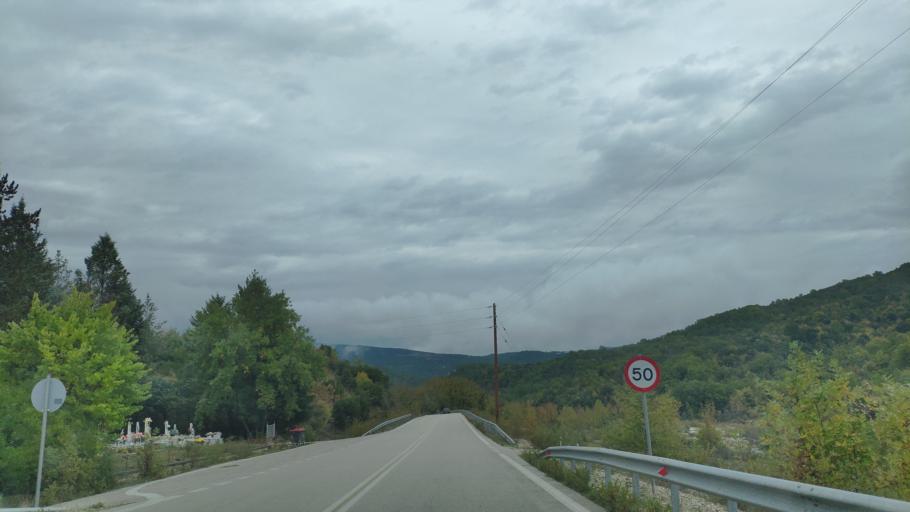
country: GR
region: Epirus
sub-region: Nomos Ioanninon
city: Pedini
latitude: 39.5250
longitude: 20.6935
